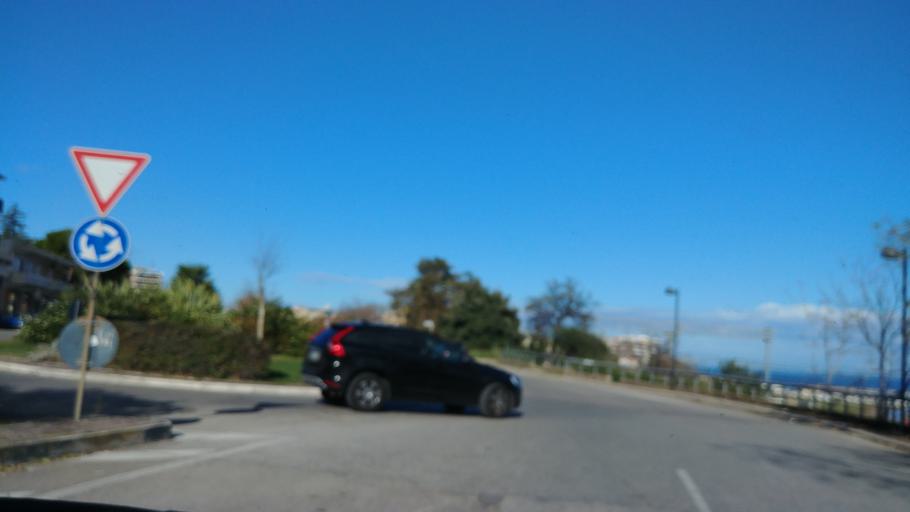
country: IT
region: Molise
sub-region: Provincia di Campobasso
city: Termoli
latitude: 41.9935
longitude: 14.9983
